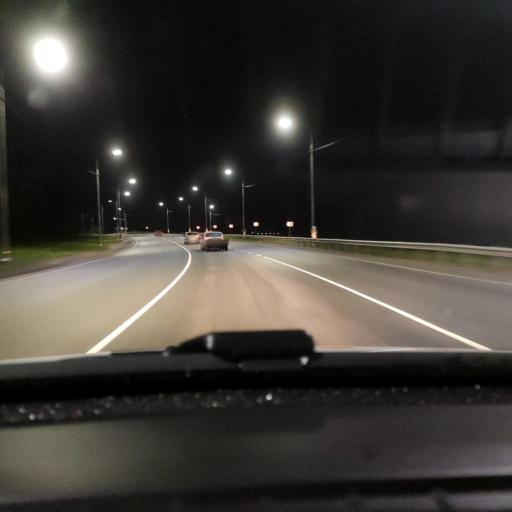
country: RU
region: Voronezj
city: Kashirskoye
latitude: 51.5009
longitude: 39.5696
